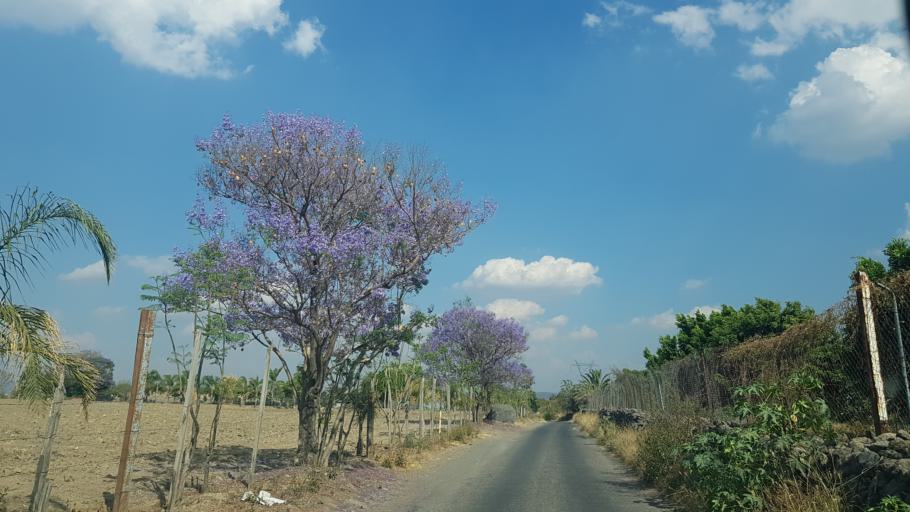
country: MX
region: Puebla
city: Atlixco
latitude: 18.8810
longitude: -98.4878
